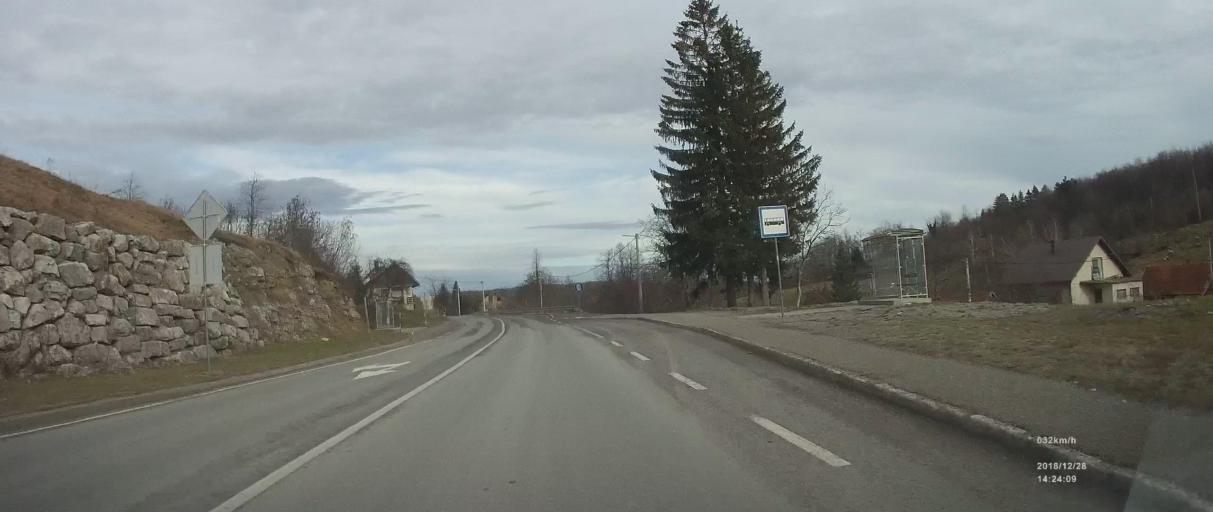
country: HR
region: Primorsko-Goranska
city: Vrbovsko
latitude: 45.3833
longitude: 15.1004
